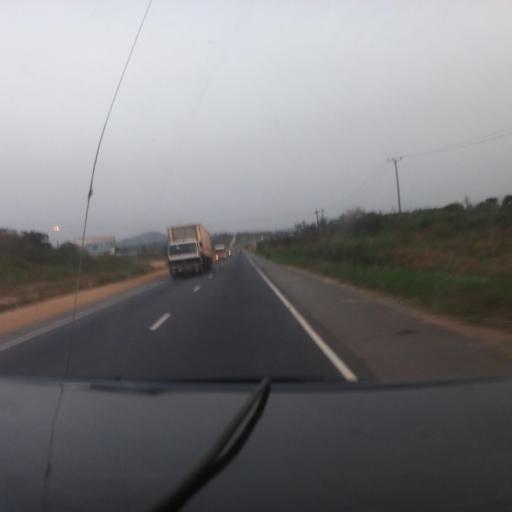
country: GH
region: Eastern
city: Nsawam
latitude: 5.8681
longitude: -0.3660
